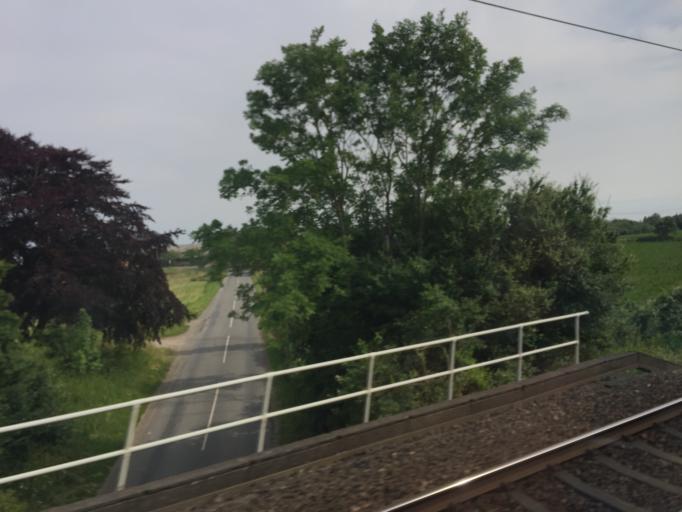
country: DK
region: South Denmark
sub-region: Odense Kommune
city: Bellinge
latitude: 55.3711
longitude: 10.2971
